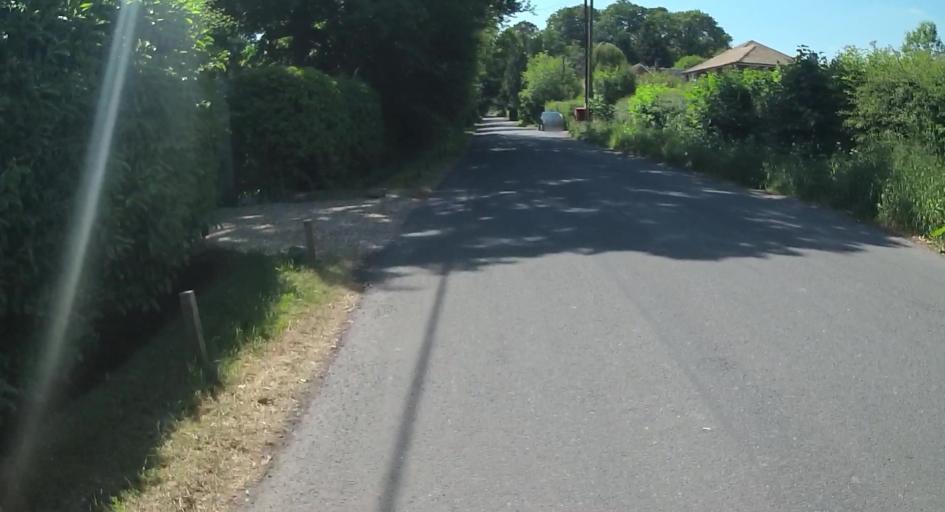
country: GB
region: England
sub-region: Hampshire
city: Tadley
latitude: 51.3137
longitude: -1.1535
